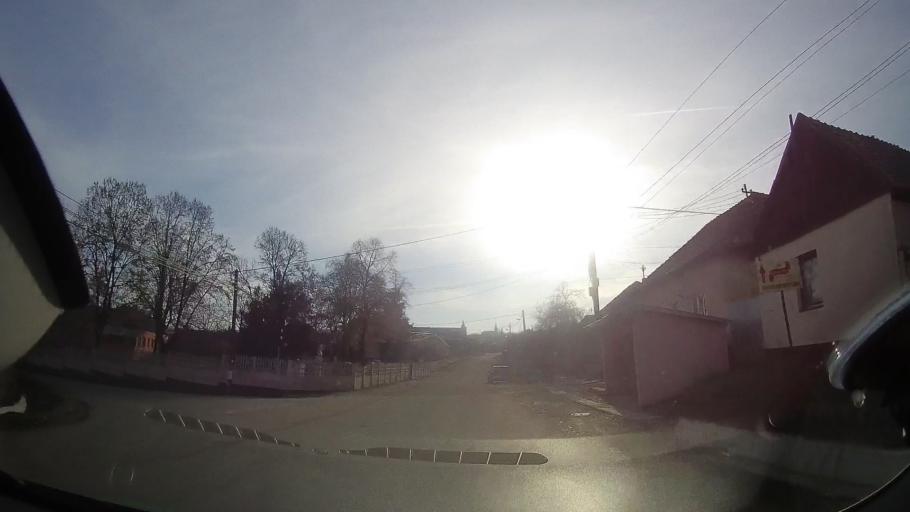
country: RO
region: Bihor
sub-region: Comuna Sarbi
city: Sarbi
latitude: 47.1931
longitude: 22.1204
